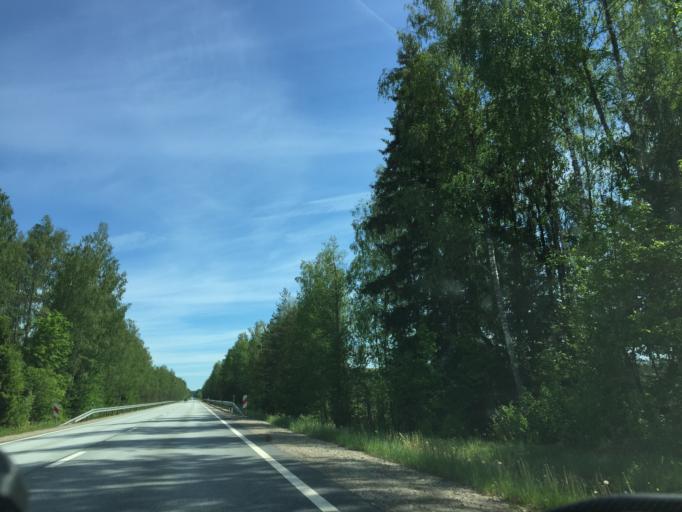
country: LV
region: Pargaujas
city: Stalbe
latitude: 57.4272
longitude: 25.1640
